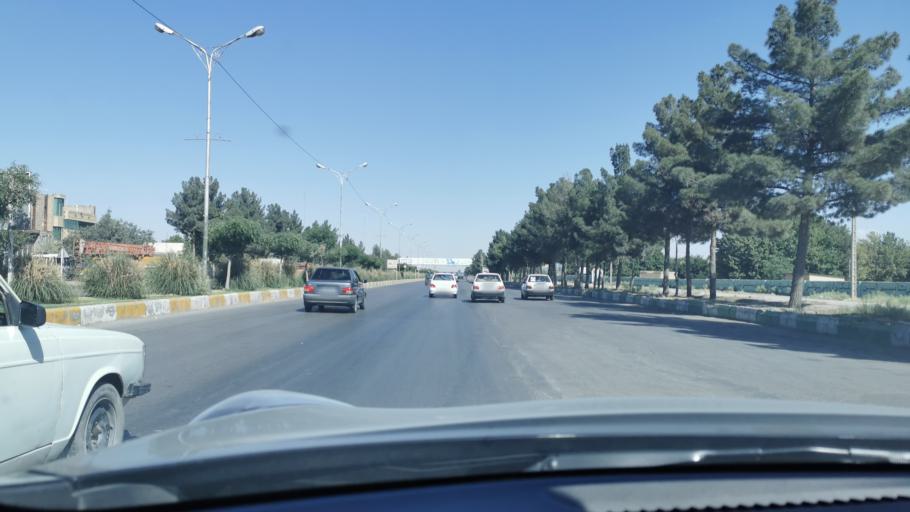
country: IR
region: Razavi Khorasan
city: Chenaran
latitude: 36.6363
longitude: 59.1264
